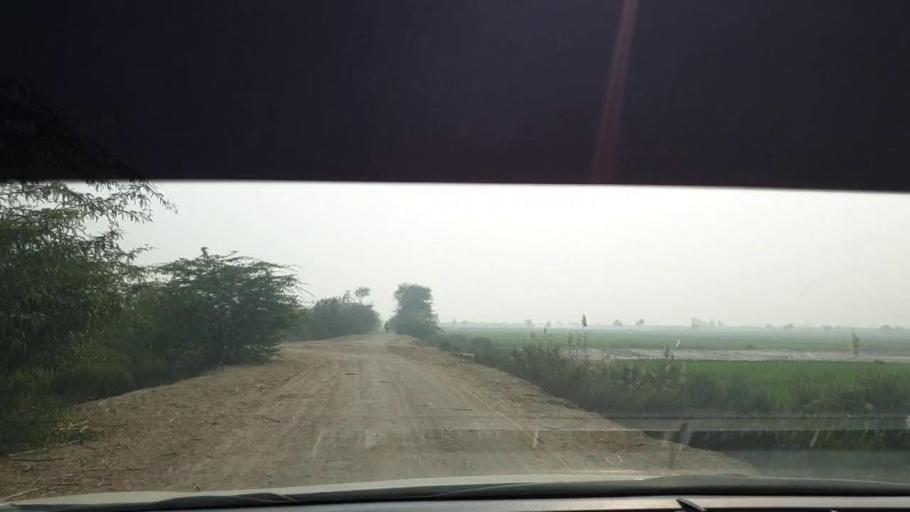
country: PK
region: Sindh
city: Berani
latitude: 25.8311
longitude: 68.8352
